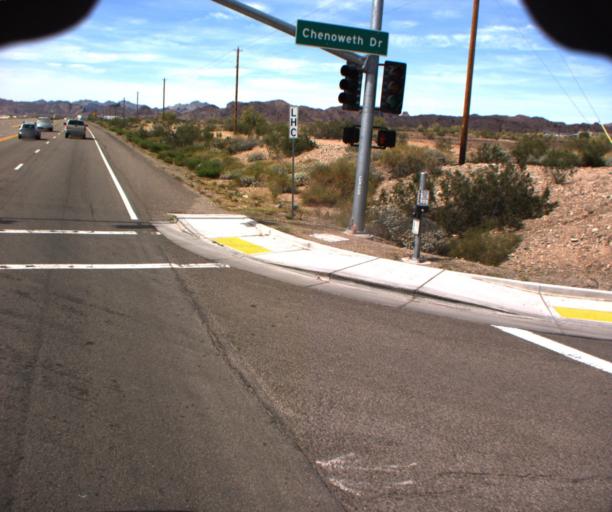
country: US
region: Arizona
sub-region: Mohave County
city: Desert Hills
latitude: 34.5464
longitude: -114.3551
